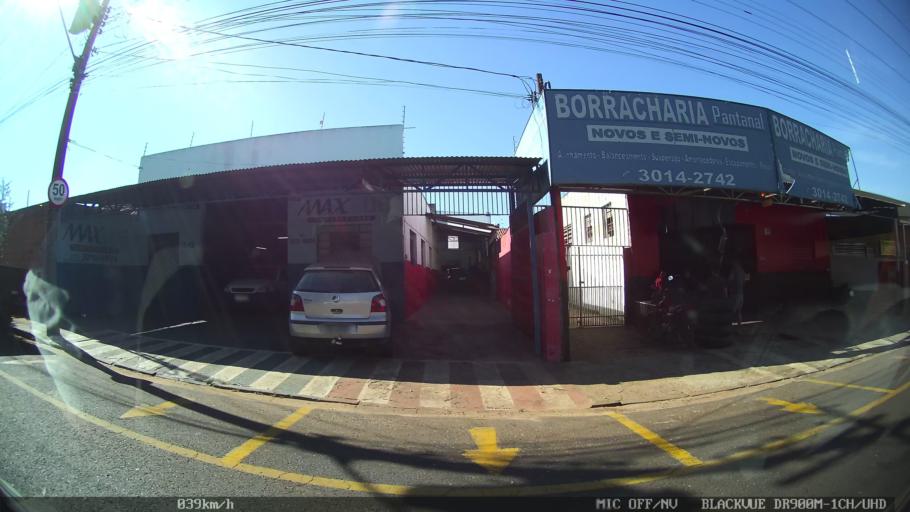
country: BR
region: Sao Paulo
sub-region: Sao Jose Do Rio Preto
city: Sao Jose do Rio Preto
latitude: -20.7844
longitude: -49.3874
